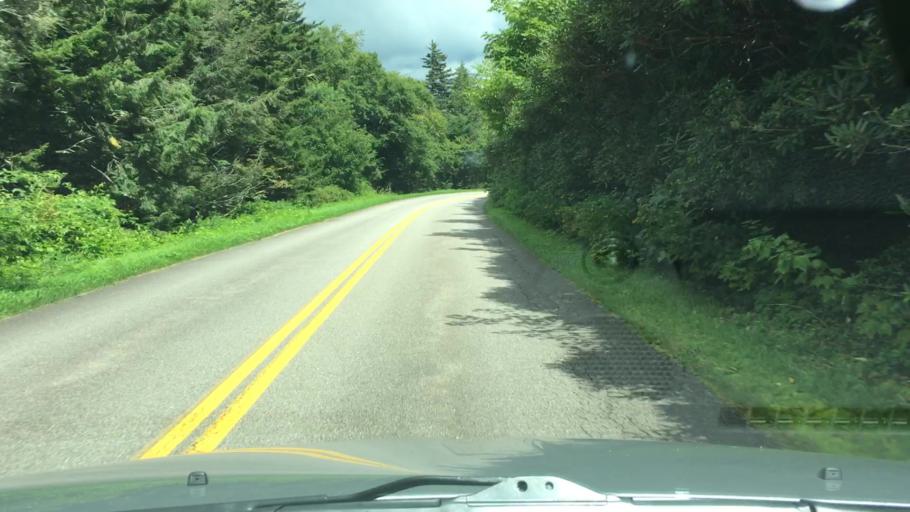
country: US
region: North Carolina
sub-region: Buncombe County
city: Black Mountain
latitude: 35.7084
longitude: -82.2655
